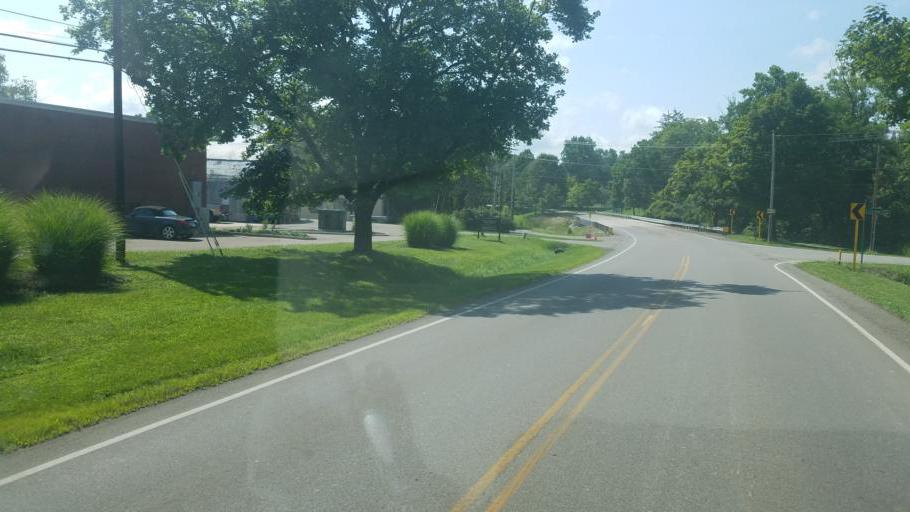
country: US
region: Ohio
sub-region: Licking County
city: Granville
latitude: 40.0779
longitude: -82.5213
